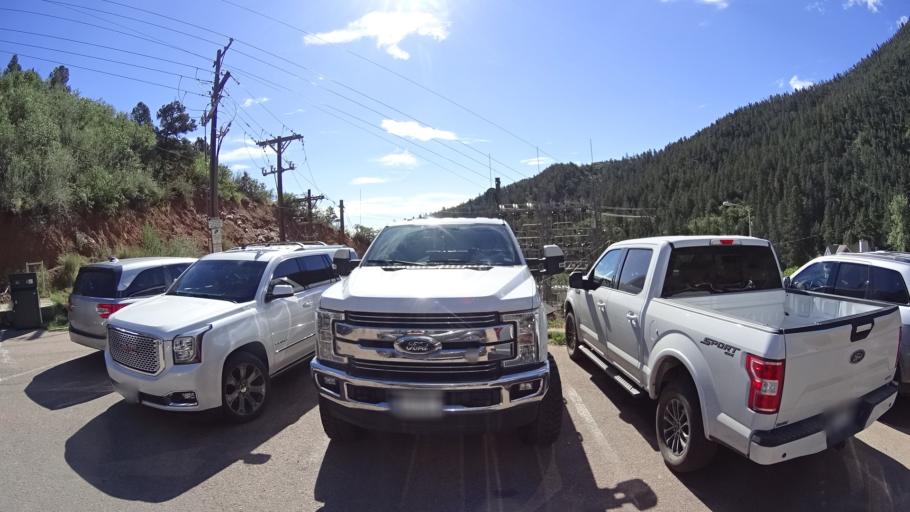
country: US
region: Colorado
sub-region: El Paso County
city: Manitou Springs
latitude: 38.8560
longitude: -104.9338
